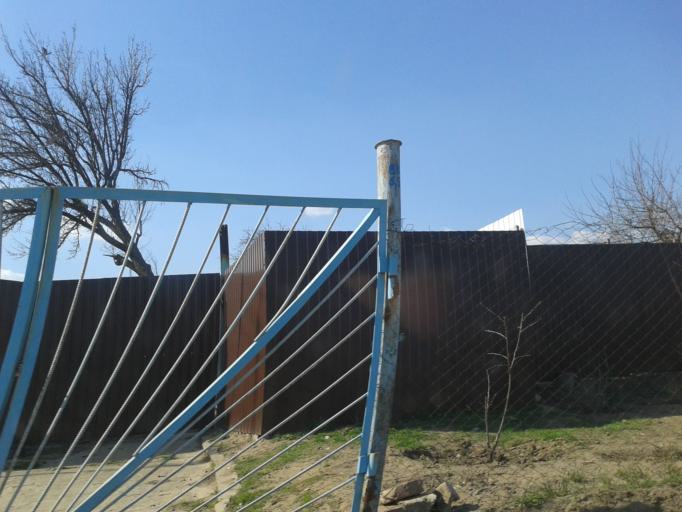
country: RU
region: Volgograd
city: Volgograd
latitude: 48.6276
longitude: 44.3810
